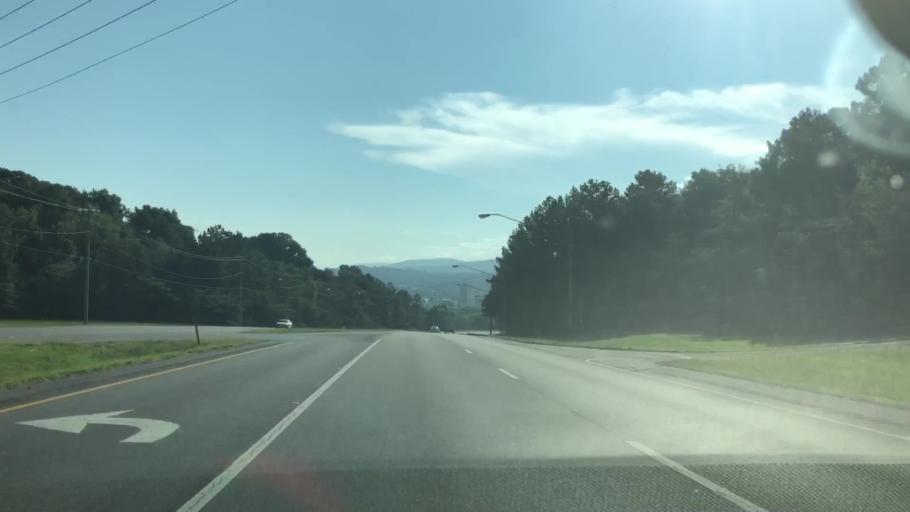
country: US
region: Alabama
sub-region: Calhoun County
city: Anniston
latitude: 33.6534
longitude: -85.8418
